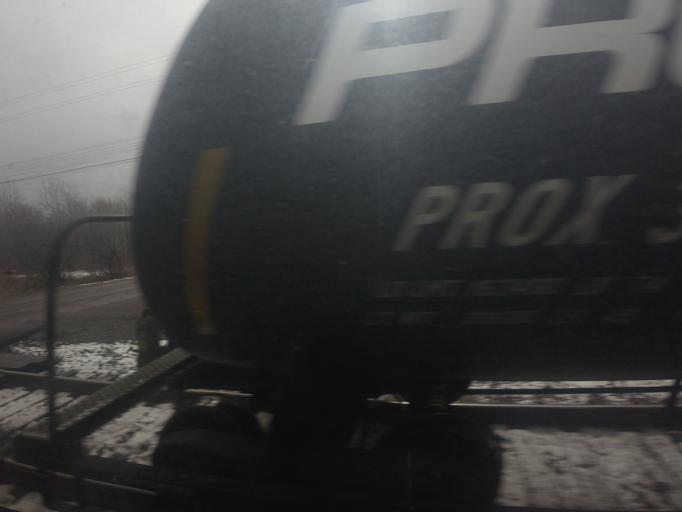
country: CA
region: Ontario
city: Quinte West
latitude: 44.0226
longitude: -77.7880
